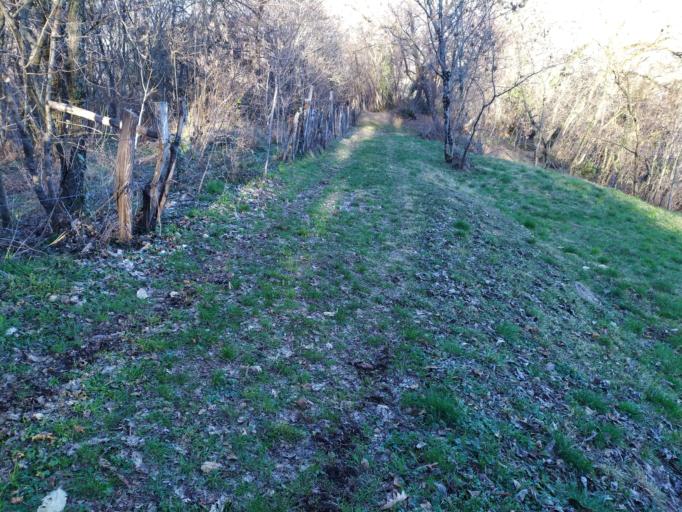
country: IT
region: Veneto
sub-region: Provincia di Vicenza
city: Monte di Malo
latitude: 45.6805
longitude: 11.3492
